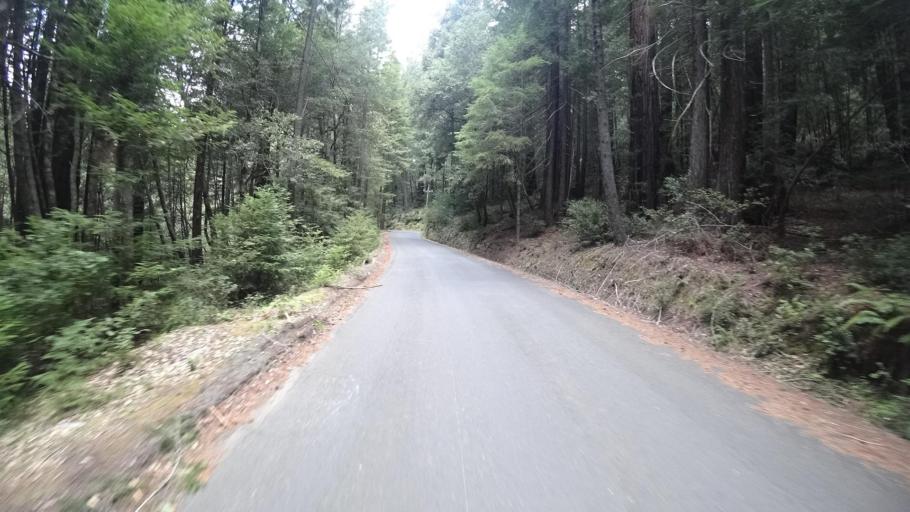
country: US
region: California
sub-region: Humboldt County
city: Redway
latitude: 39.9988
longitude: -123.9279
